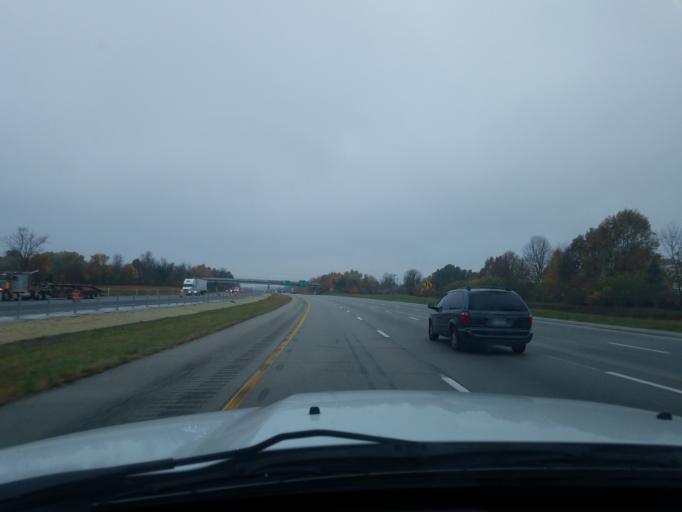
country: US
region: Kentucky
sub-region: Hardin County
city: Elizabethtown
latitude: 37.7303
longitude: -85.8170
